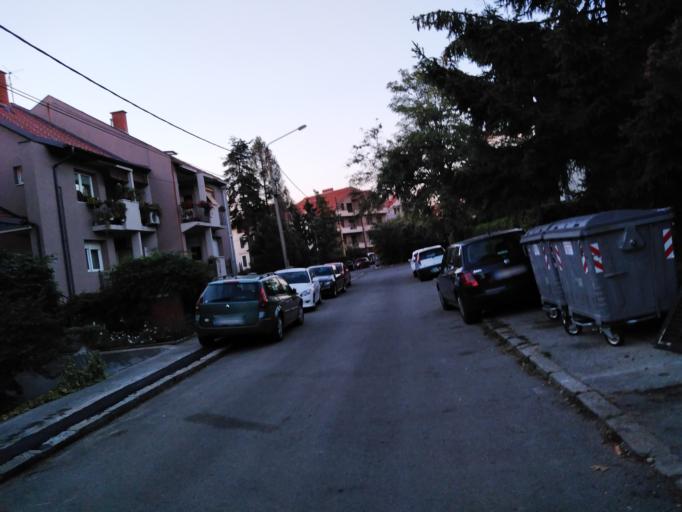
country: RS
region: Central Serbia
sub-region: Belgrade
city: Rakovica
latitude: 44.7515
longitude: 20.4212
